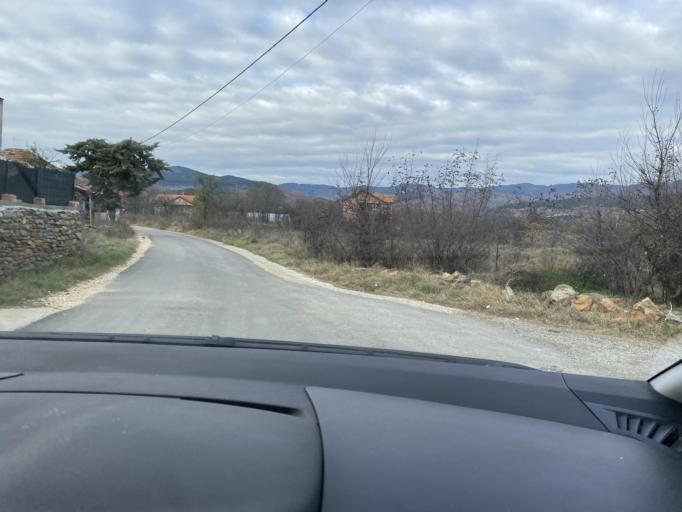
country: MK
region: Opstina Rankovce
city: Rankovce
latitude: 42.1847
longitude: 22.1083
